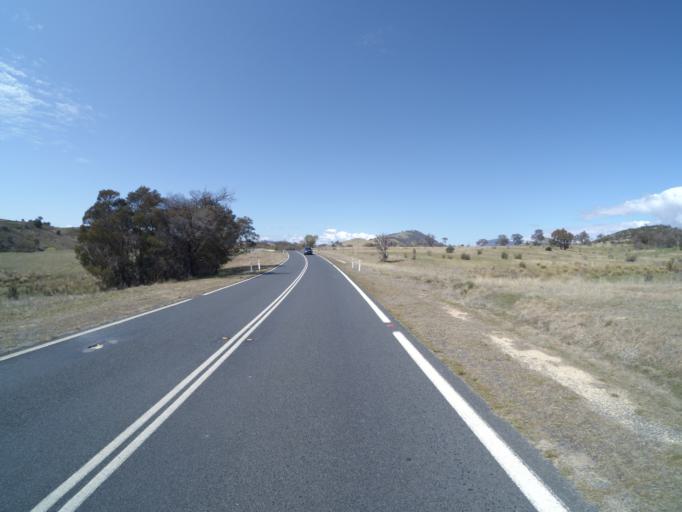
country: AU
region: Australian Capital Territory
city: Macarthur
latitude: -35.4590
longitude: 149.0167
